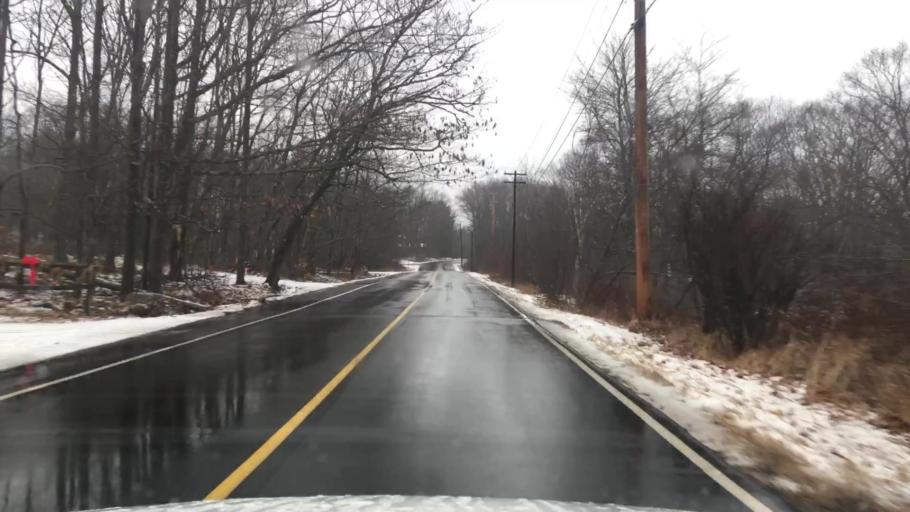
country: US
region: Maine
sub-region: York County
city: Arundel
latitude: 43.4099
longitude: -70.4124
